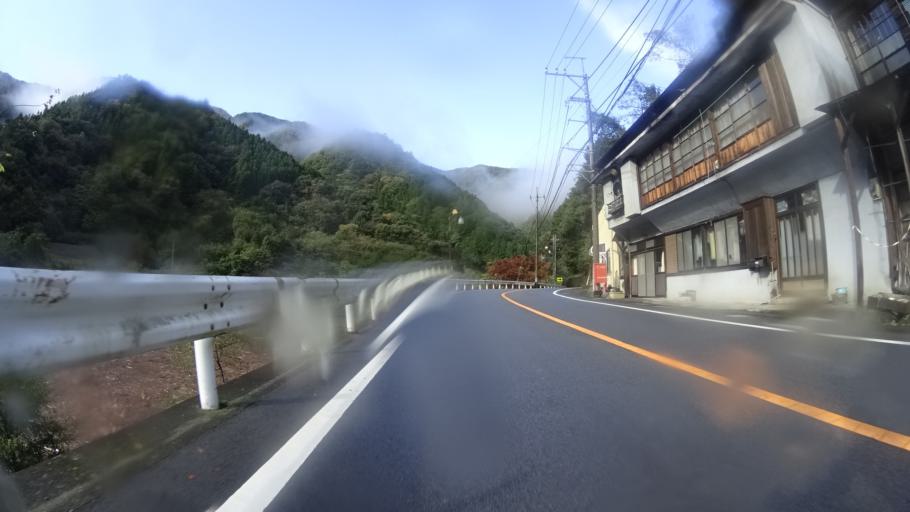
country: JP
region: Yamanashi
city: Otsuki
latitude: 35.7791
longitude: 138.9824
